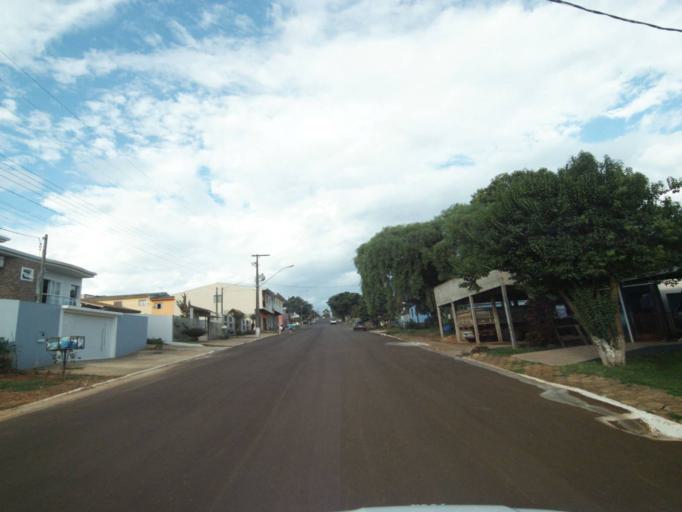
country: BR
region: Parana
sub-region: Laranjeiras Do Sul
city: Laranjeiras do Sul
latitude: -25.4928
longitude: -52.5286
